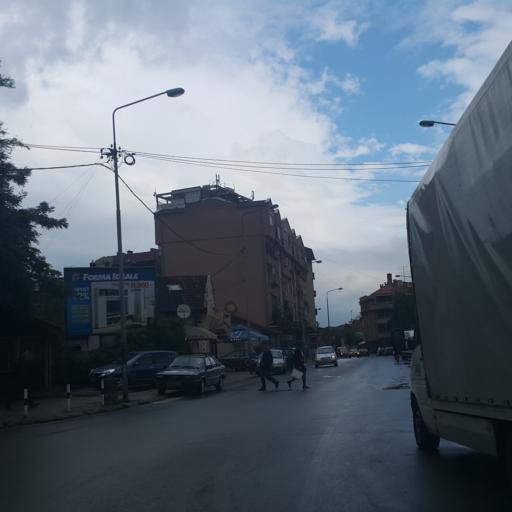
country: RS
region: Central Serbia
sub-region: Rasinski Okrug
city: Krusevac
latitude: 43.5774
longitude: 21.3358
